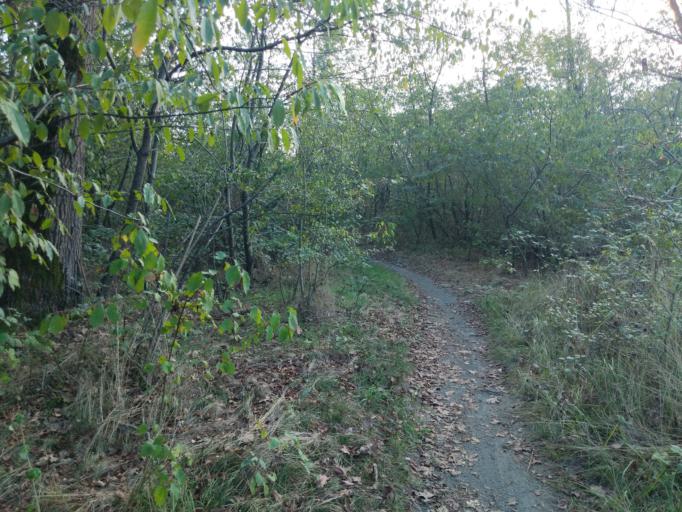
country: IT
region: Lombardy
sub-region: Citta metropolitana di Milano
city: Turbigo
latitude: 45.5214
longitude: 8.7229
